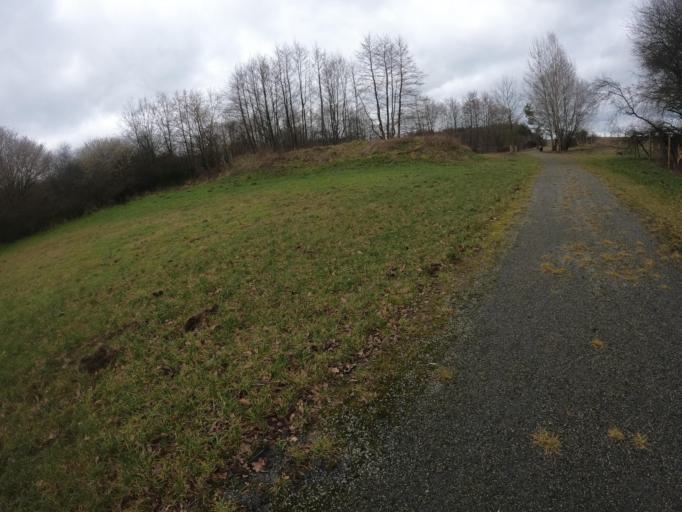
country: PL
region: West Pomeranian Voivodeship
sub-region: Powiat kolobrzeski
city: Goscino
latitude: 54.0418
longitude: 15.6688
